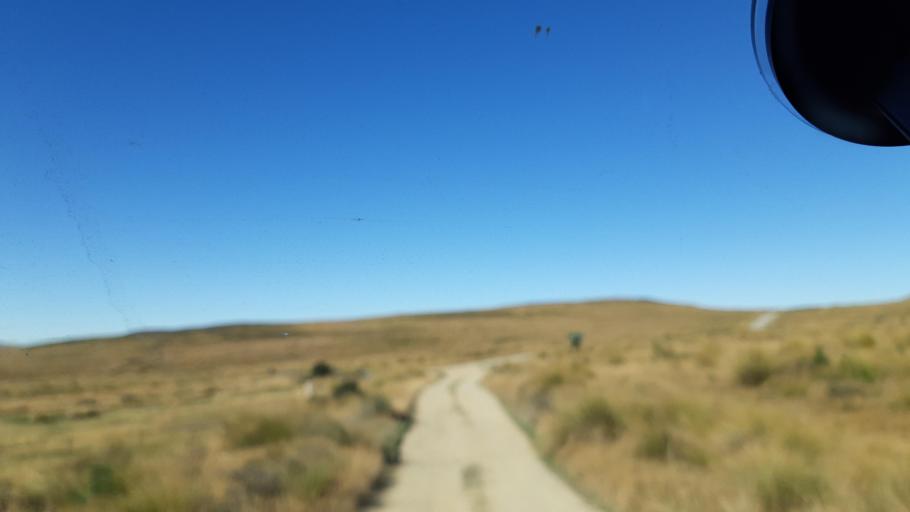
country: NZ
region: Otago
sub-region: Queenstown-Lakes District
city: Wanaka
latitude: -44.7771
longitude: 169.8893
